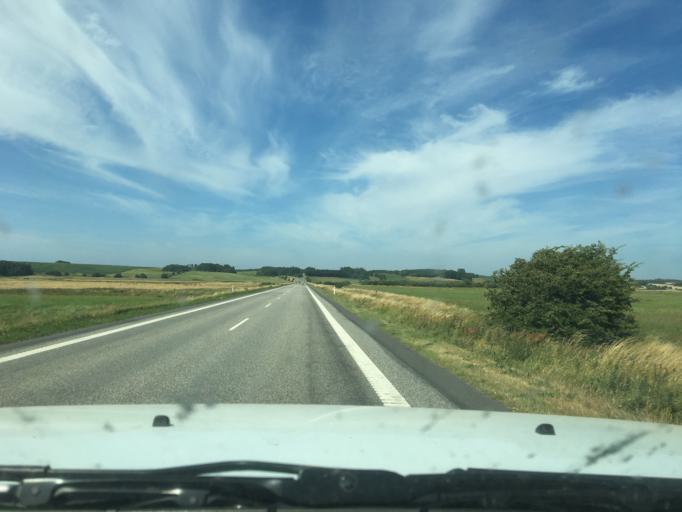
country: DK
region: Central Jutland
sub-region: Viborg Kommune
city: Viborg
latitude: 56.5331
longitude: 9.4038
